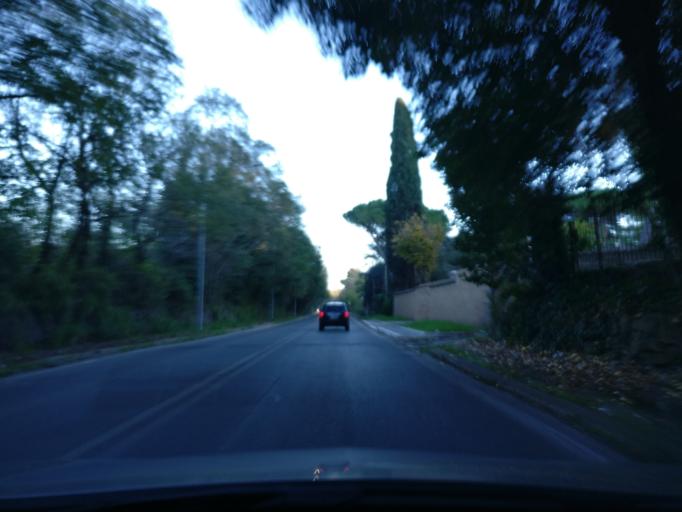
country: IT
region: Latium
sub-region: Citta metropolitana di Roma Capitale
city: Rome
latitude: 41.8505
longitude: 12.5304
